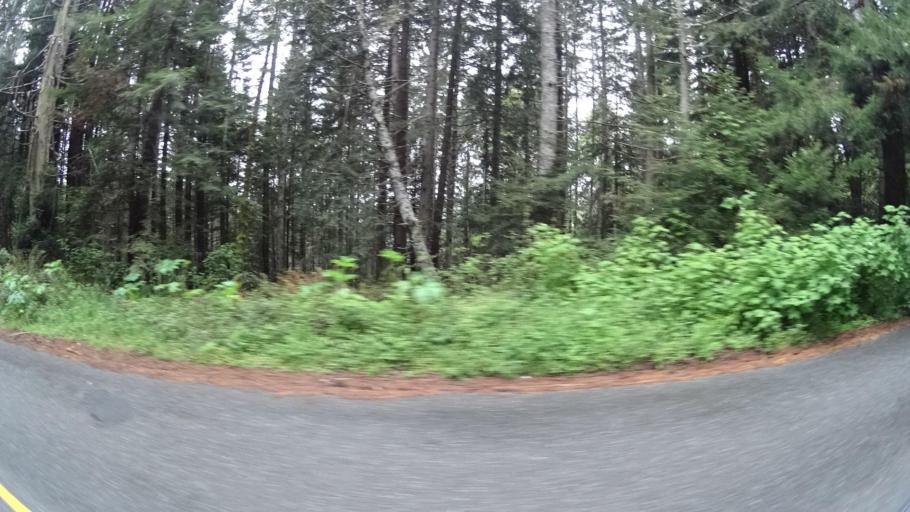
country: US
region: California
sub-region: Humboldt County
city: Westhaven-Moonstone
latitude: 41.2983
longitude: -124.0185
